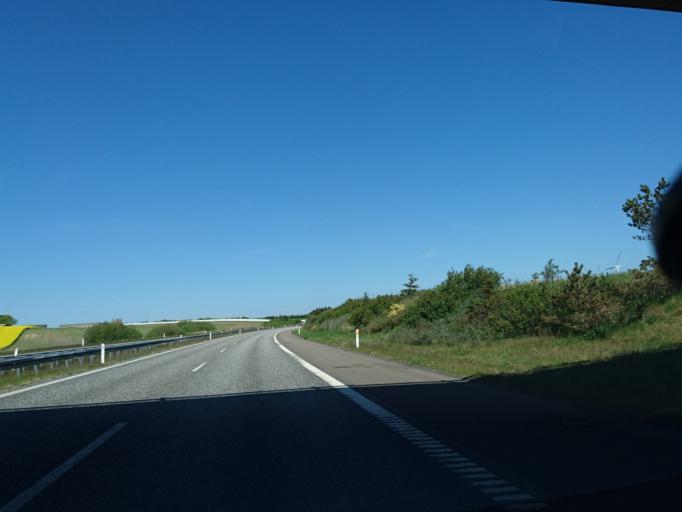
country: DK
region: North Denmark
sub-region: Hjorring Kommune
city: Hirtshals
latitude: 57.5436
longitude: 10.0062
